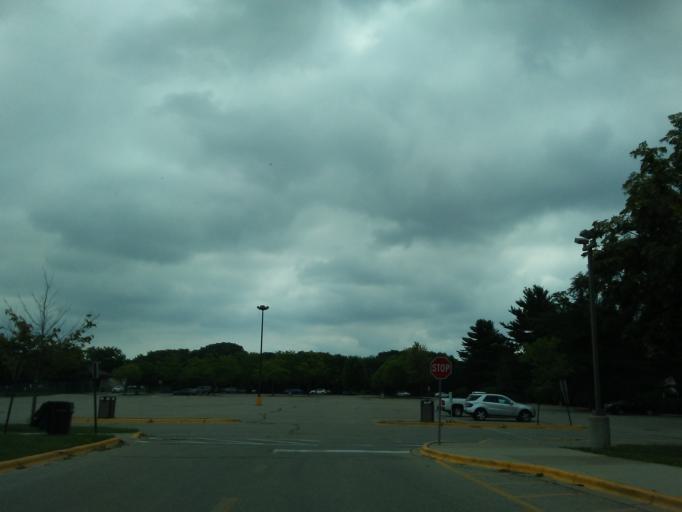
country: US
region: Wisconsin
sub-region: Dane County
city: Middleton
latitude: 43.1011
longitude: -89.5069
